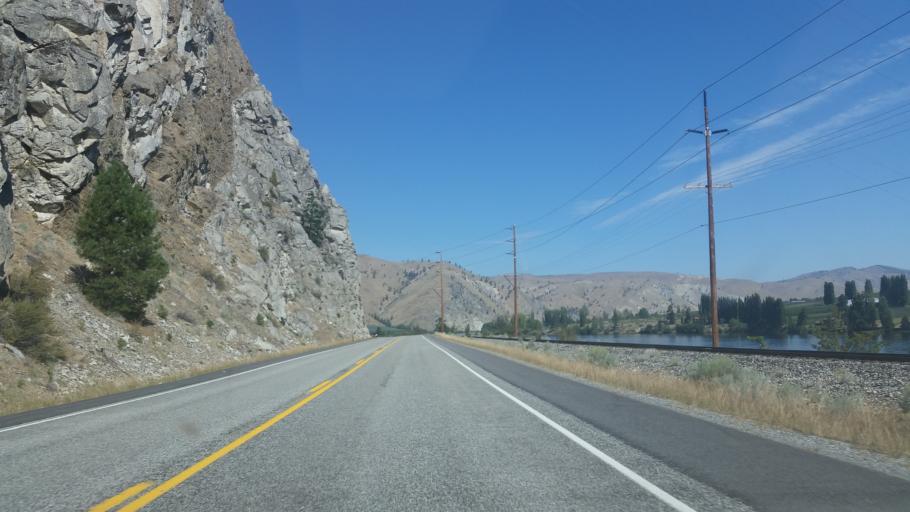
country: US
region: Washington
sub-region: Chelan County
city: Entiat
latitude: 47.7073
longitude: -120.2152
